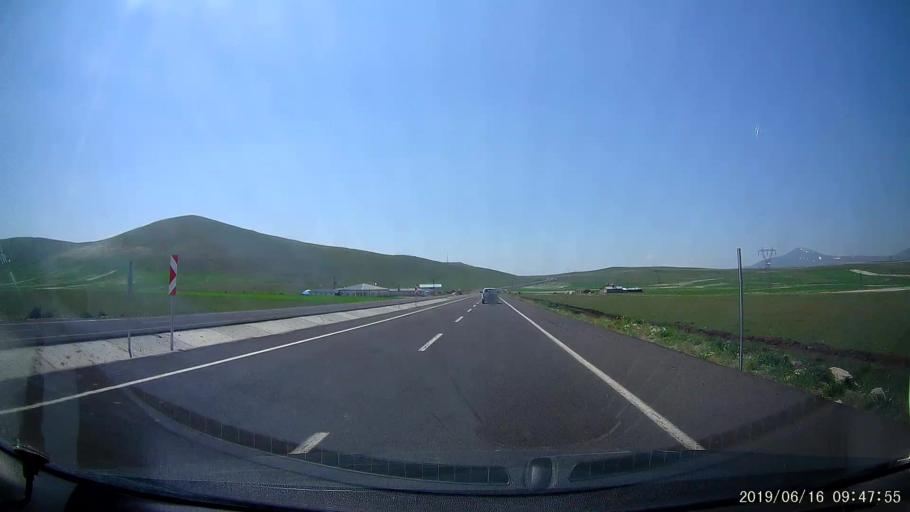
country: TR
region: Kars
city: Digor
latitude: 40.4395
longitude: 43.3491
